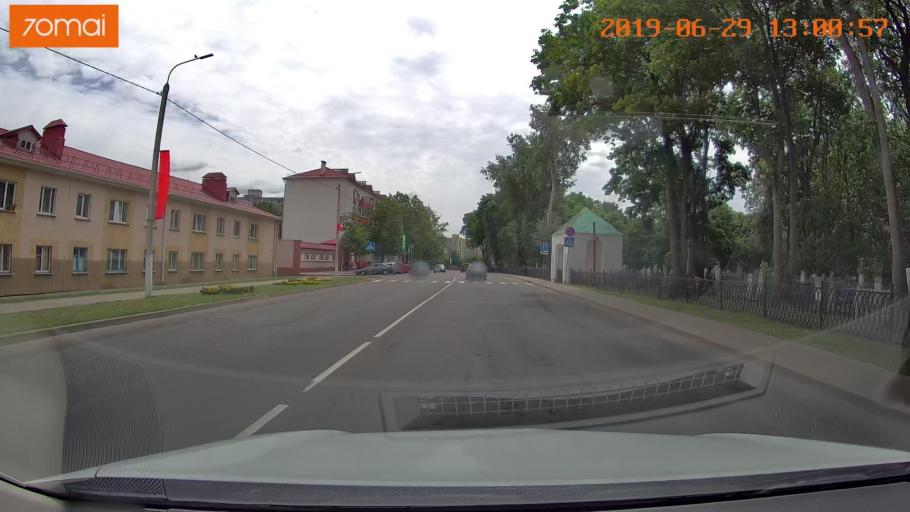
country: BY
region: Minsk
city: Slutsk
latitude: 53.0413
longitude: 27.5587
